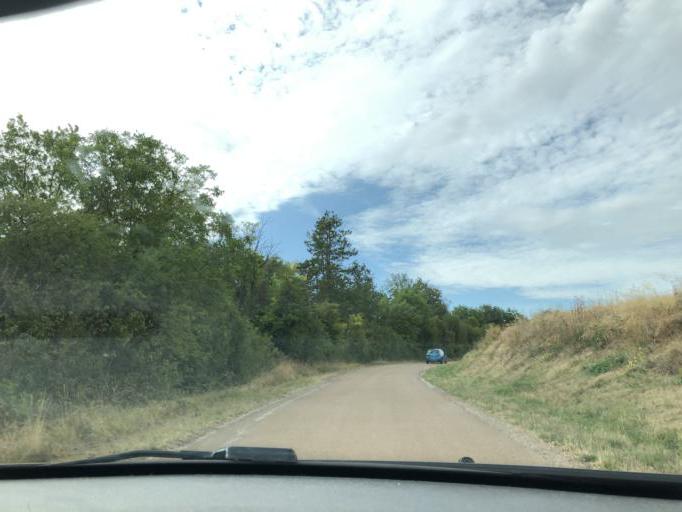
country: FR
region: Bourgogne
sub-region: Departement de l'Yonne
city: Chablis
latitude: 47.7840
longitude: 3.8340
